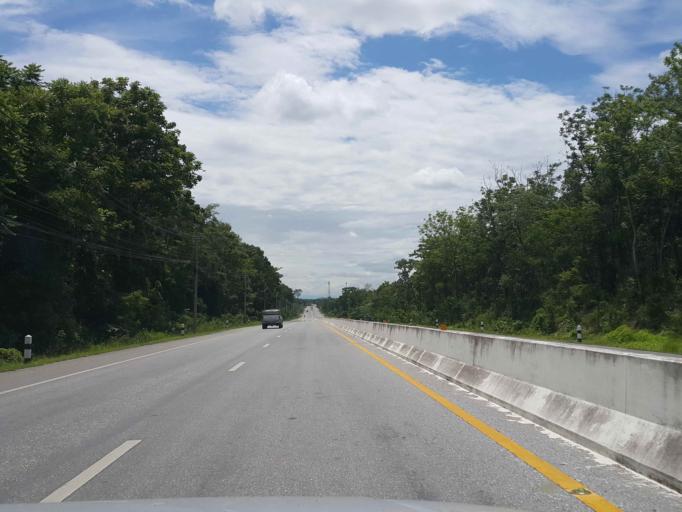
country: TH
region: Sukhothai
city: Ban Dan Lan Hoi
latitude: 17.0032
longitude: 99.5143
